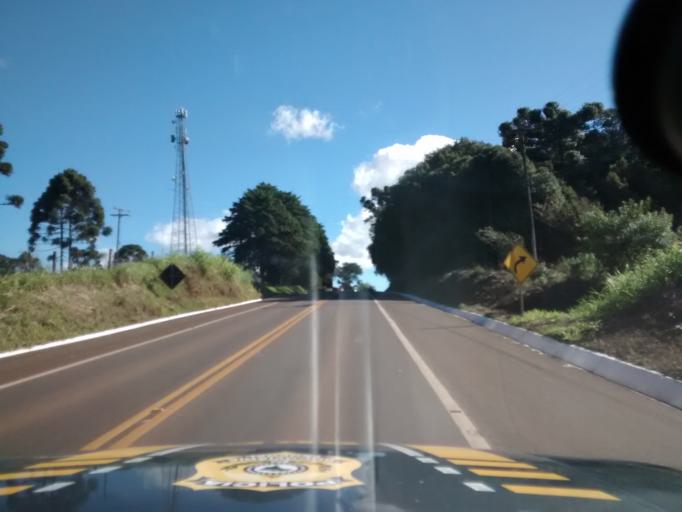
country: BR
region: Rio Grande do Sul
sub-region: Vacaria
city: Vacaria
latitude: -28.3240
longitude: -51.1939
